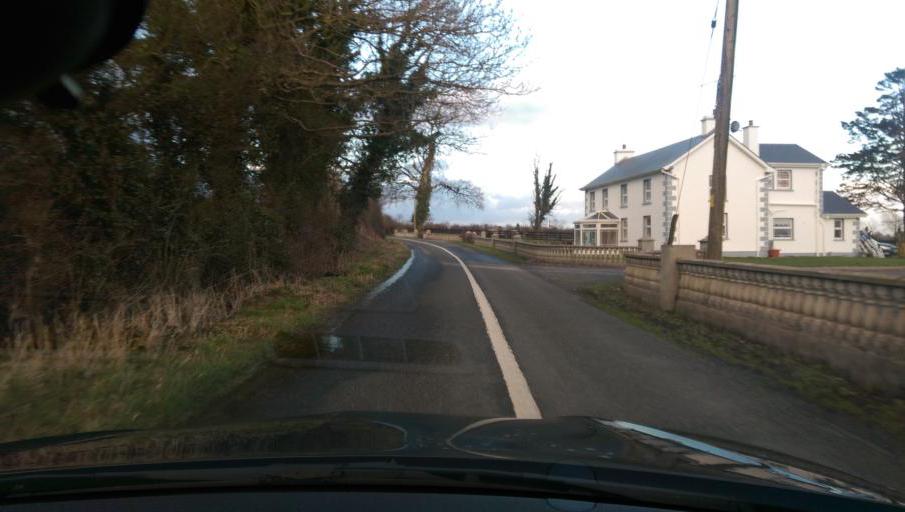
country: IE
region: Connaught
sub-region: County Galway
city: Ballinasloe
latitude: 53.4597
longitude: -8.3764
